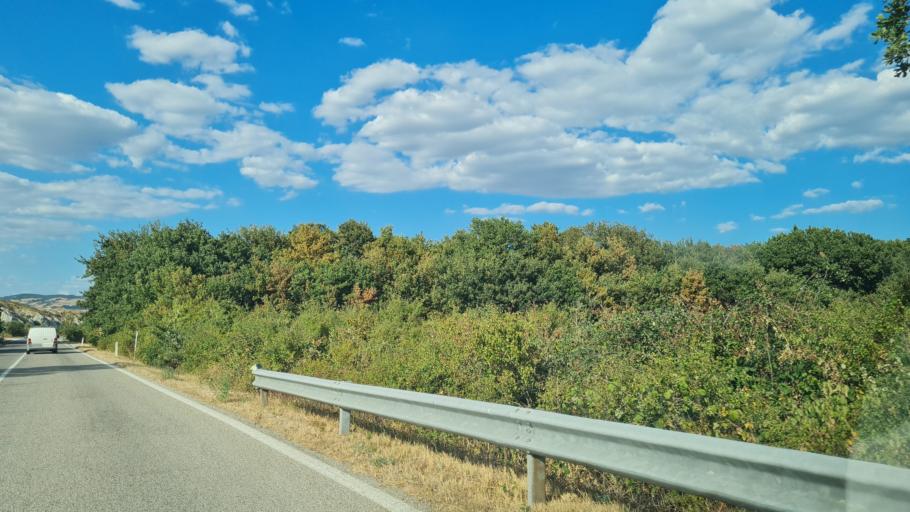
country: IT
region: Tuscany
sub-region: Provincia di Siena
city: Castiglione d'Orcia
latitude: 42.9827
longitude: 11.7120
